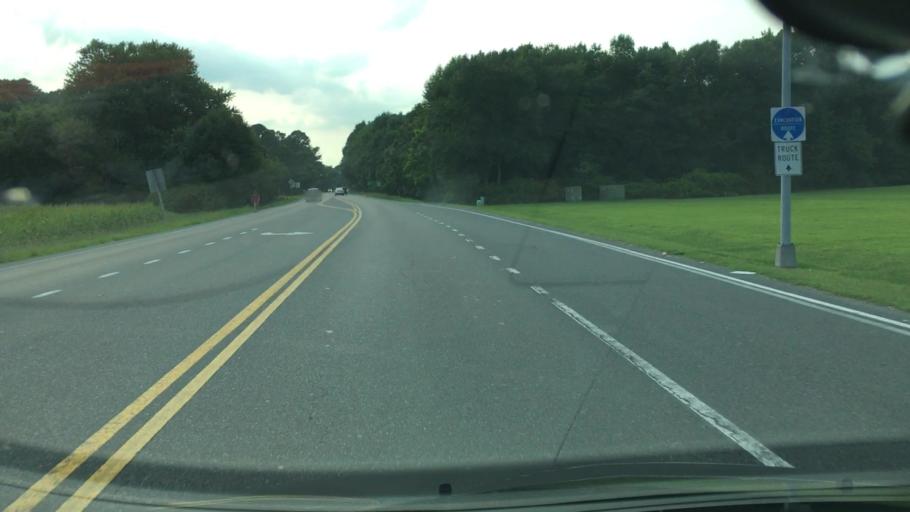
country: US
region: Maryland
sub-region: Worcester County
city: Ocean Pines
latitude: 38.3841
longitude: -75.1778
